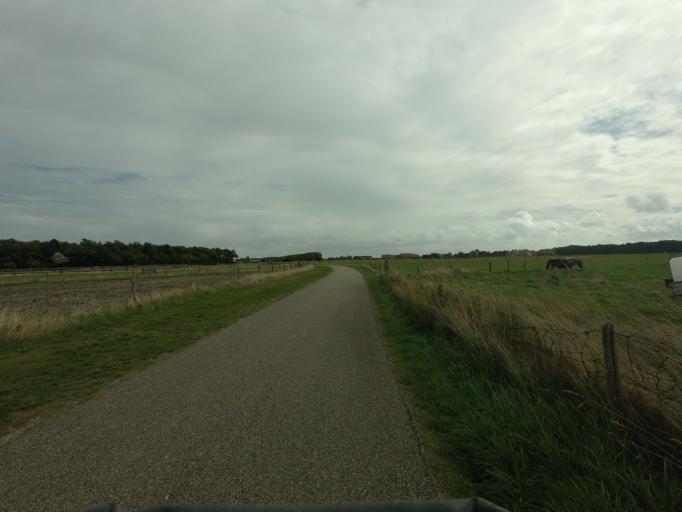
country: NL
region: Friesland
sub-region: Gemeente Ameland
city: Nes
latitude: 53.4525
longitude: 5.7926
